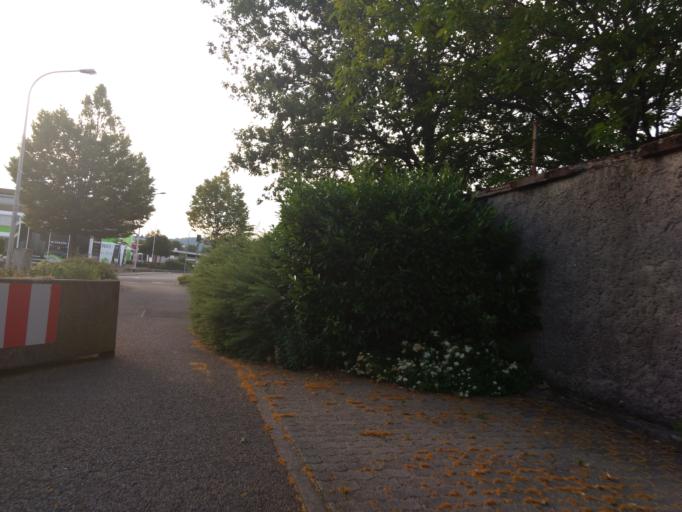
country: DE
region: Saarland
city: Saarlouis
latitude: 49.3113
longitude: 6.7373
